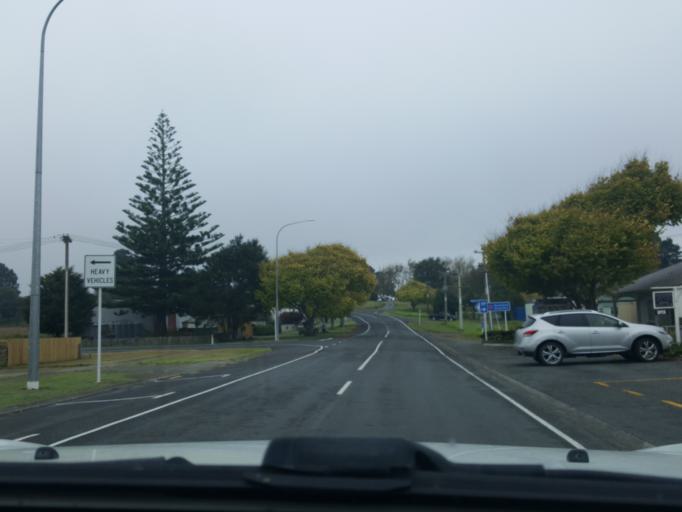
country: NZ
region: Waikato
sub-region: Waikato District
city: Te Kauwhata
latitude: -37.4314
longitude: 175.1342
